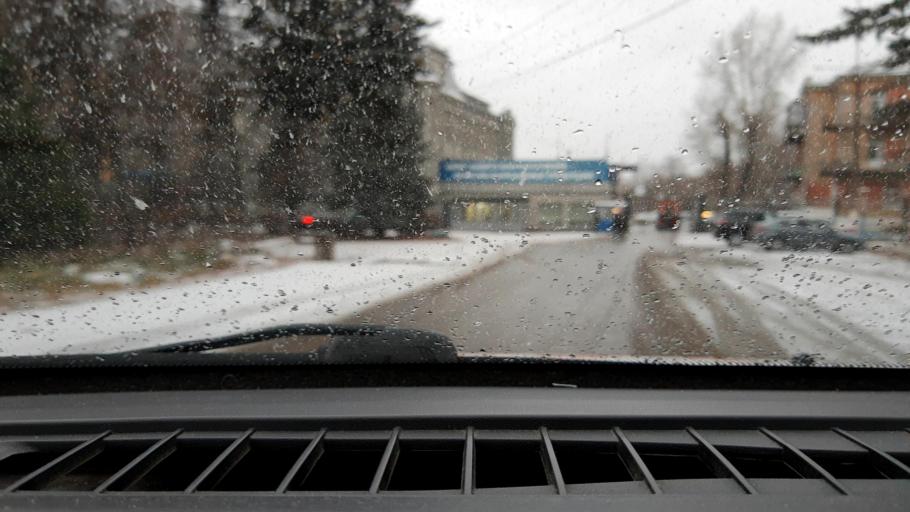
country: RU
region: Nizjnij Novgorod
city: Nizhniy Novgorod
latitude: 56.2647
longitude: 43.9322
